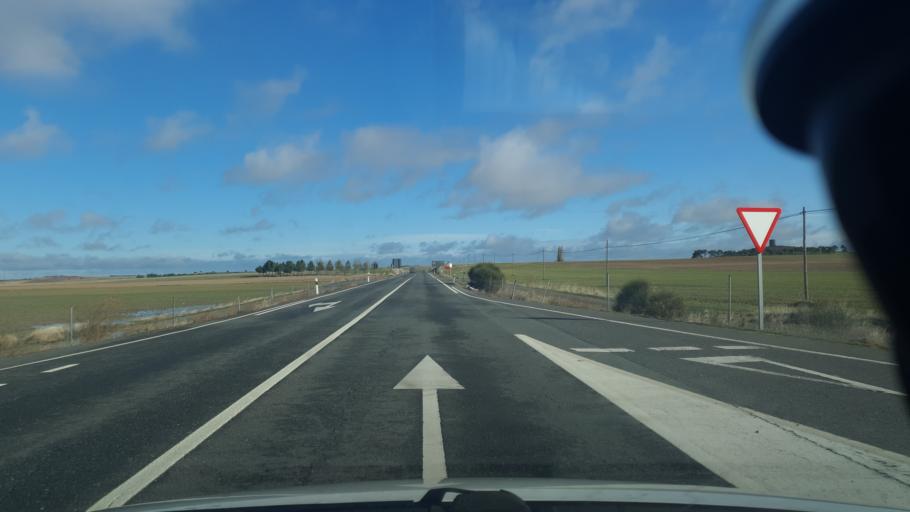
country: ES
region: Castille and Leon
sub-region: Provincia de Segovia
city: Codorniz
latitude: 41.0520
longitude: -4.6234
